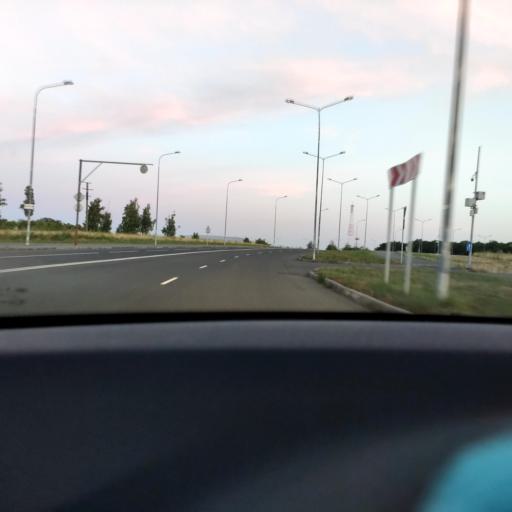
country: RU
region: Samara
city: Samara
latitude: 53.2891
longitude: 50.2347
